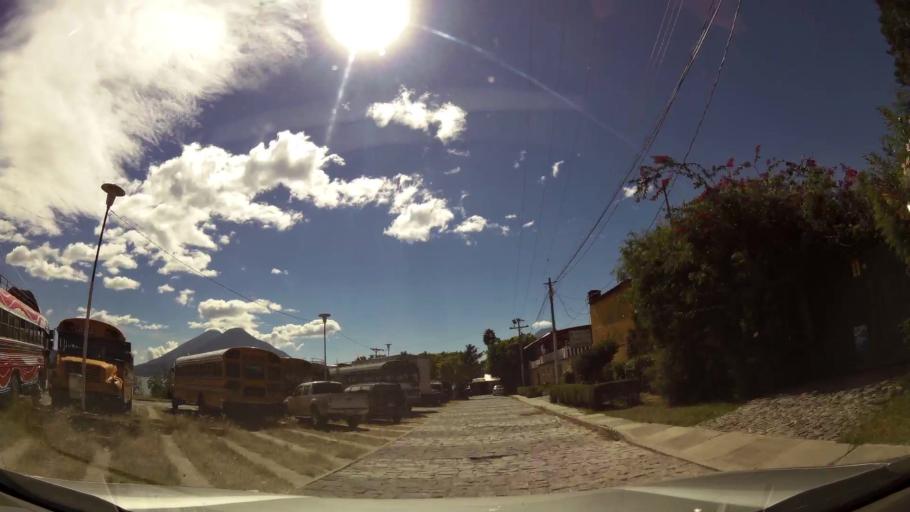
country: GT
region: Solola
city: Panajachel
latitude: 14.7364
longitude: -91.1573
